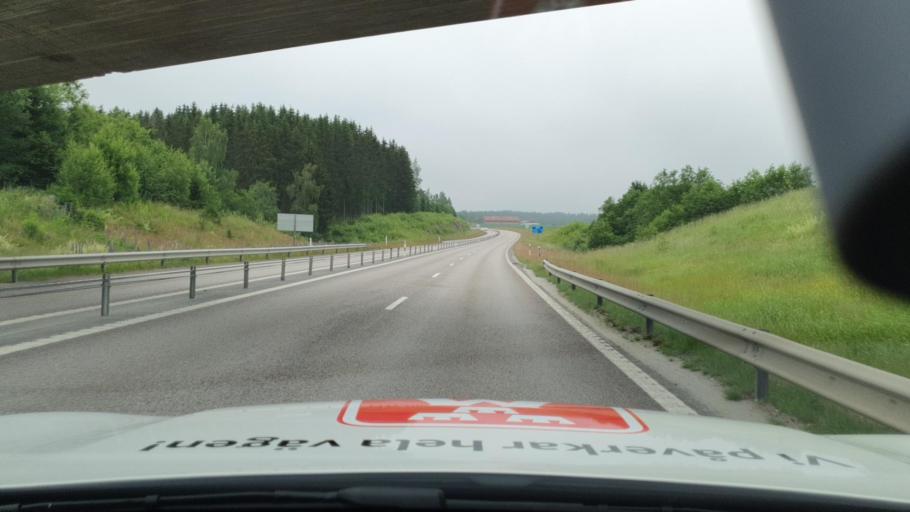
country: SE
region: Vaermland
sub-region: Karlstads Kommun
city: Edsvalla
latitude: 59.5203
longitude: 13.2146
